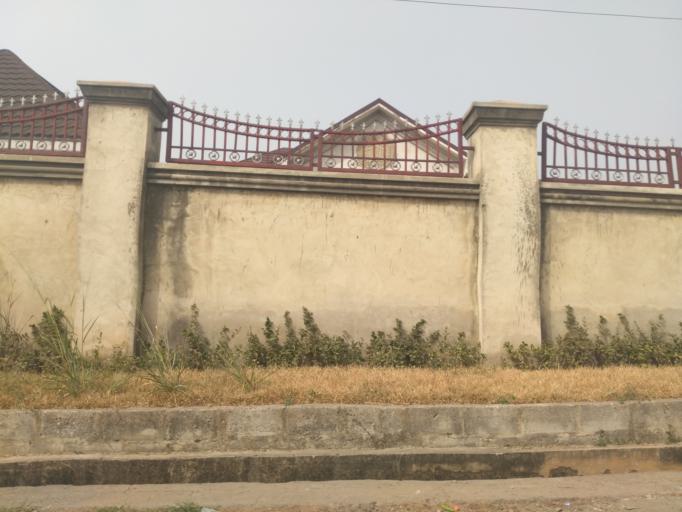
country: GH
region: Ashanti
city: Kumasi
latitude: 6.6778
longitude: -1.6066
